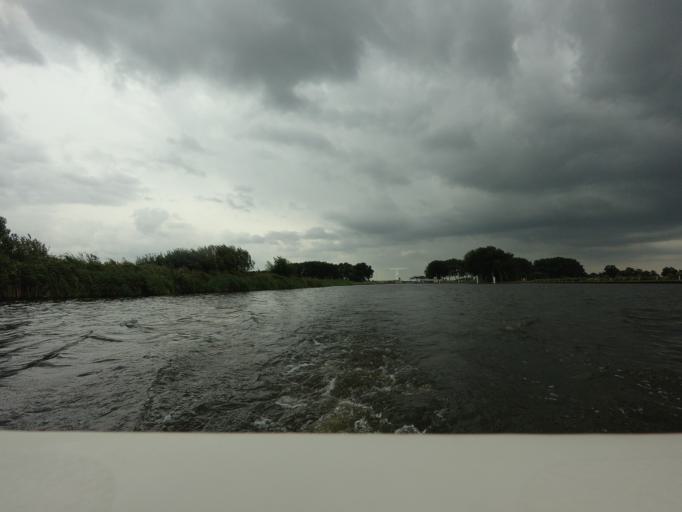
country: NL
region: Friesland
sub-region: Gemeente Smallingerland
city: Oudega
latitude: 53.1074
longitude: 5.9486
